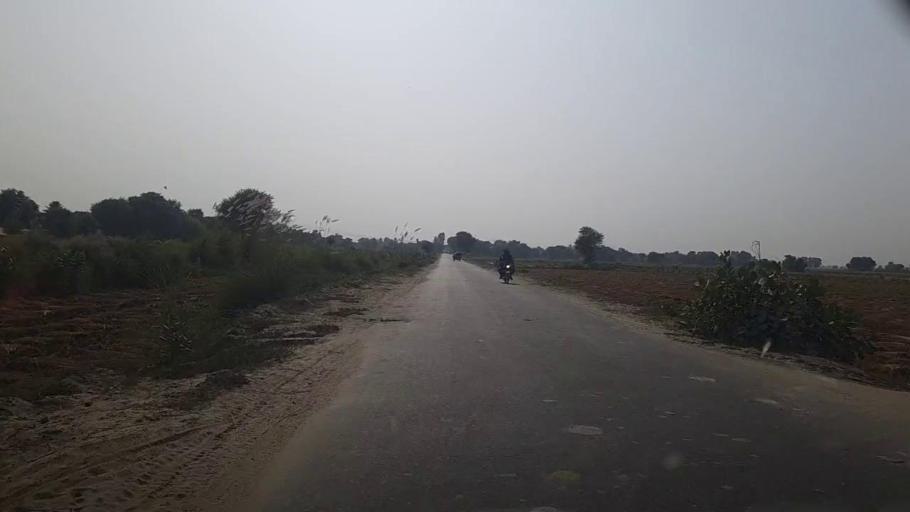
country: PK
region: Sindh
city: Kashmor
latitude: 28.3988
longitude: 69.5478
